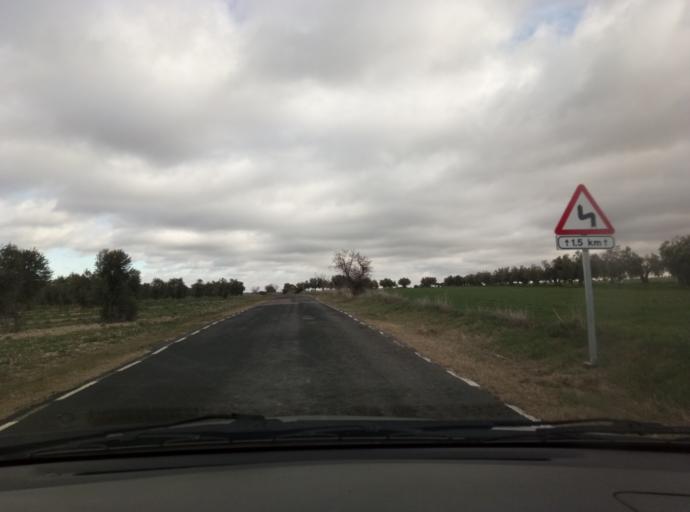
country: ES
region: Catalonia
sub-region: Provincia de Lleida
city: Vallbona de les Monges
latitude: 41.5705
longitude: 1.0709
